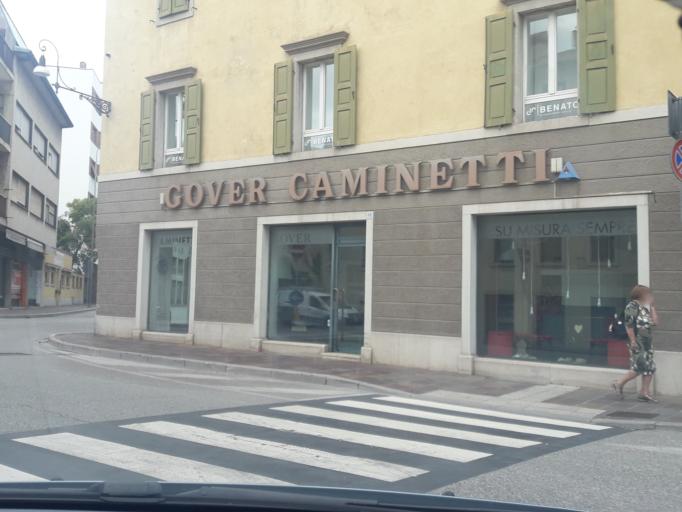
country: IT
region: Friuli Venezia Giulia
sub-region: Provincia di Udine
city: Udine
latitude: 46.0602
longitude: 13.2336
